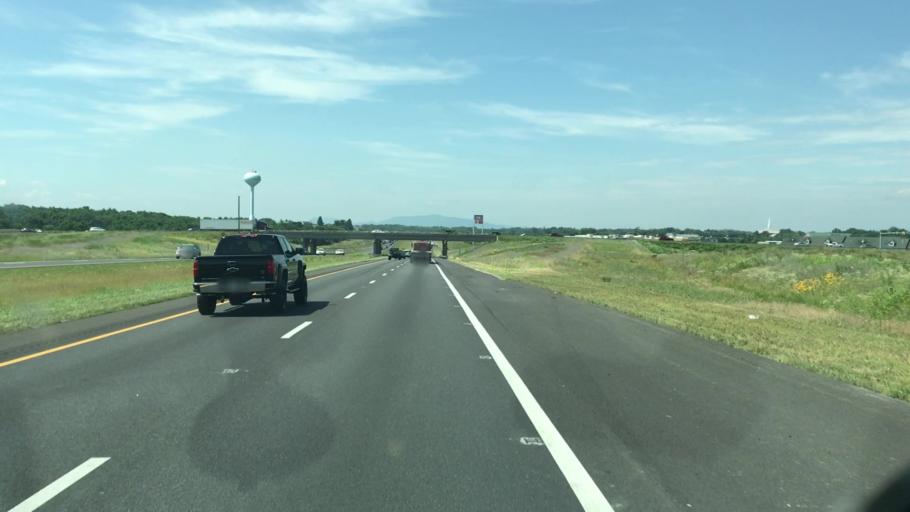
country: US
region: Virginia
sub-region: Frederick County
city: Stephens City
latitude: 39.1228
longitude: -78.1897
